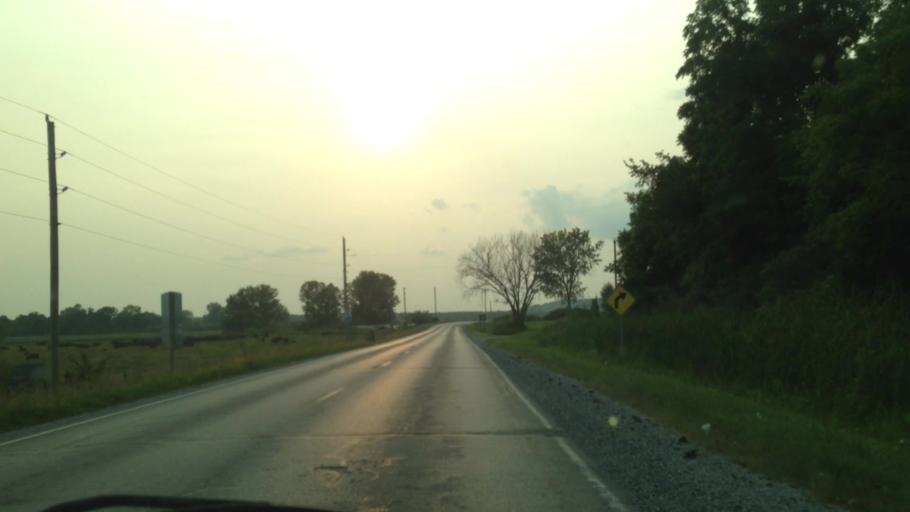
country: US
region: Iowa
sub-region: Iowa County
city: Marengo
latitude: 41.8234
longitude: -92.0650
